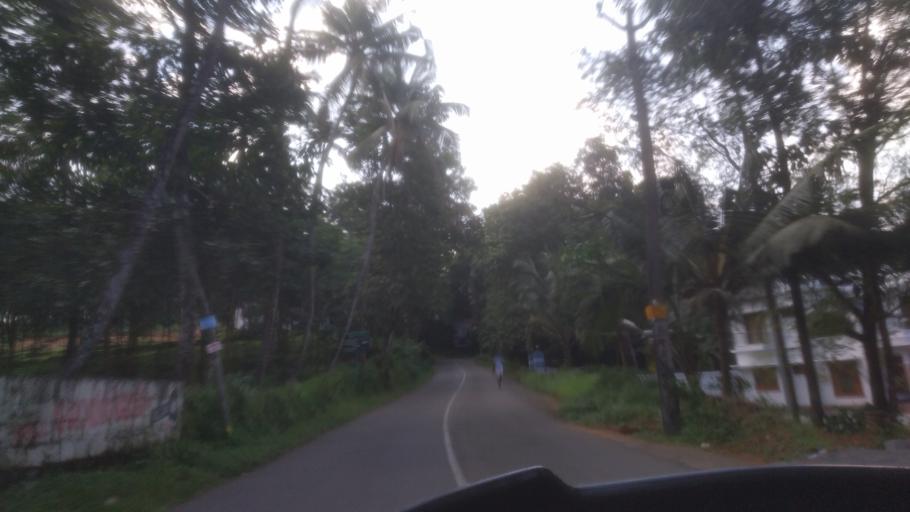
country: IN
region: Kerala
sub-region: Ernakulam
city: Kotamangalam
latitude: 10.0058
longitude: 76.6770
